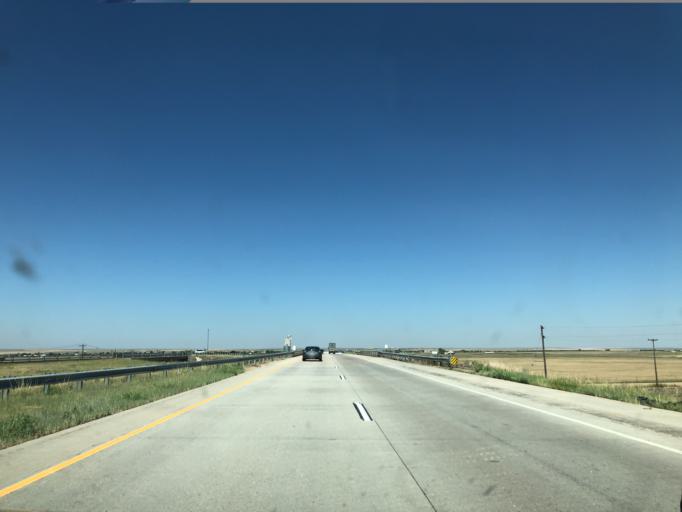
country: US
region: Colorado
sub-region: Arapahoe County
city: Byers
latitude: 39.7044
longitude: -104.1893
